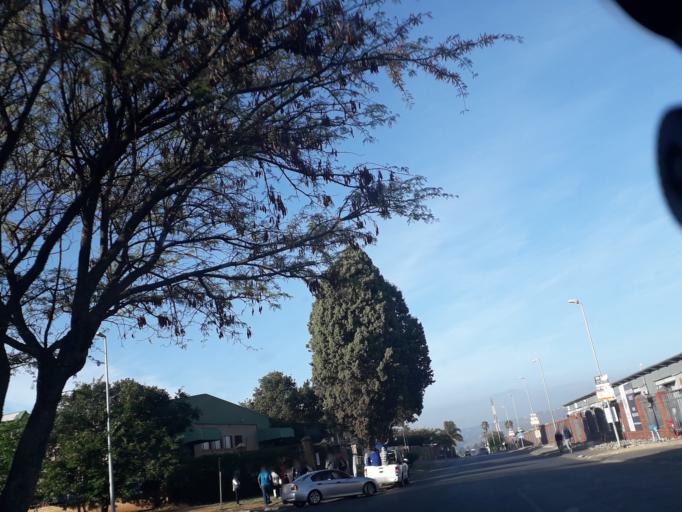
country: ZA
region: Gauteng
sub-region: West Rand District Municipality
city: Muldersdriseloop
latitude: -26.0773
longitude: 27.9168
